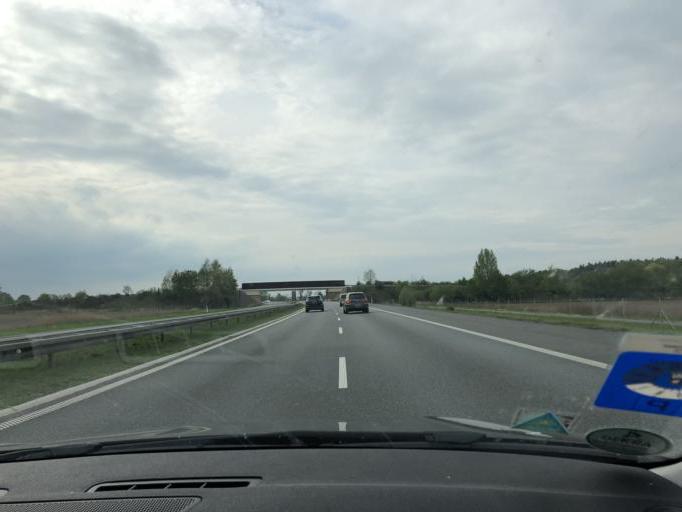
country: PL
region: Opole Voivodeship
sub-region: Powiat brzeski
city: Lewin Brzeski
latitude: 50.7053
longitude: 17.6132
